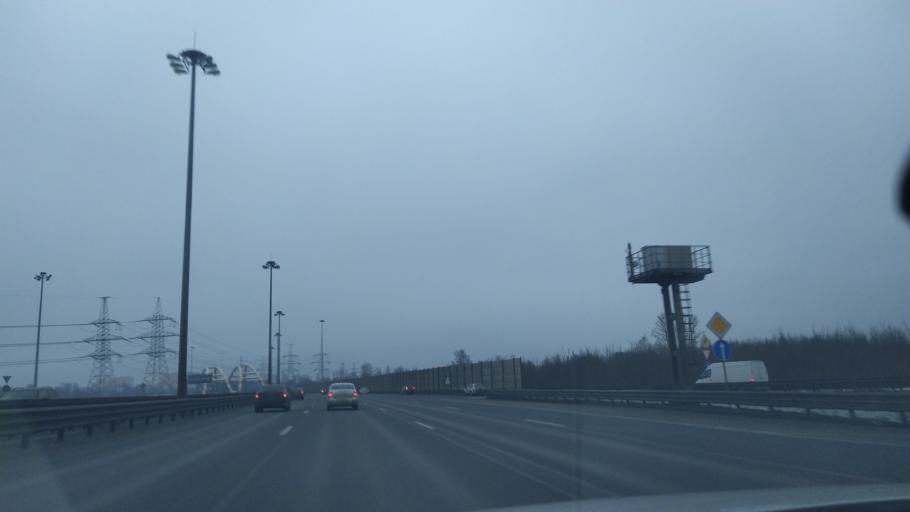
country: RU
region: St.-Petersburg
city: Krasnogvargeisky
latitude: 59.9894
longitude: 30.4844
